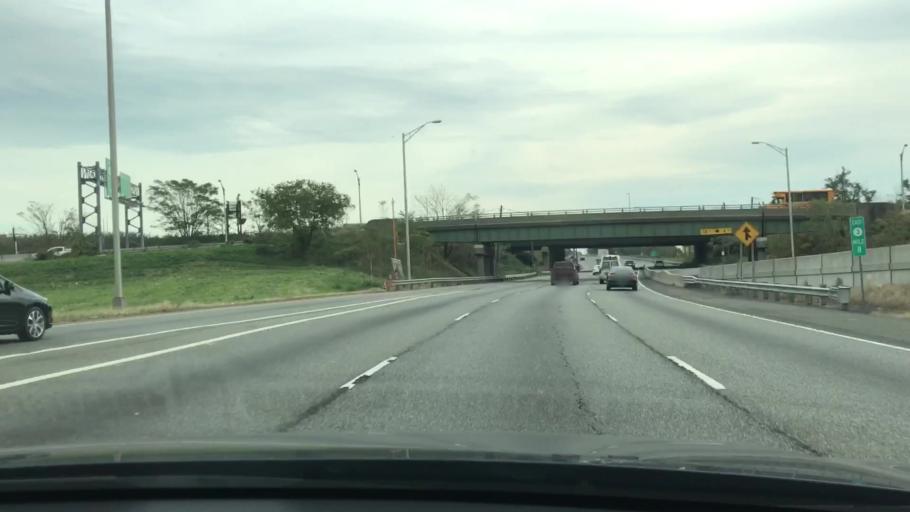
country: US
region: New Jersey
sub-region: Hudson County
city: Secaucus
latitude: 40.8041
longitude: -74.0735
